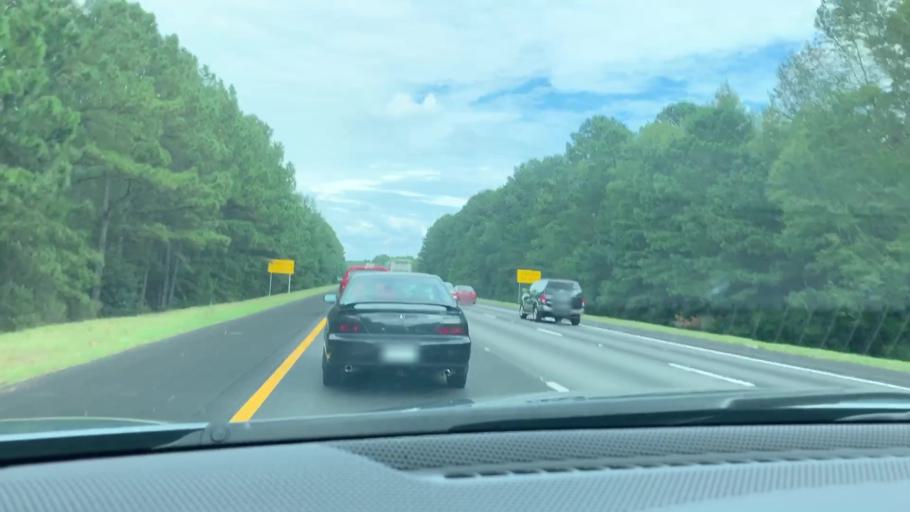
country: US
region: Georgia
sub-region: Chatham County
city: Pooler
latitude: 32.1607
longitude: -81.2244
